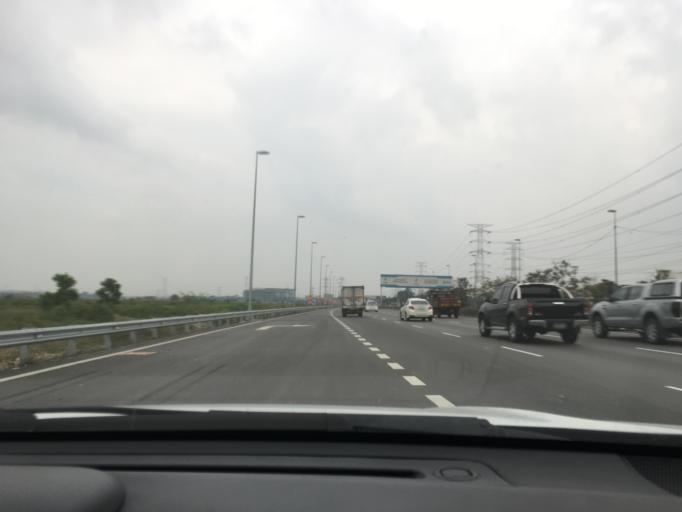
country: MY
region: Selangor
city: Klang
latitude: 3.0944
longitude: 101.4434
